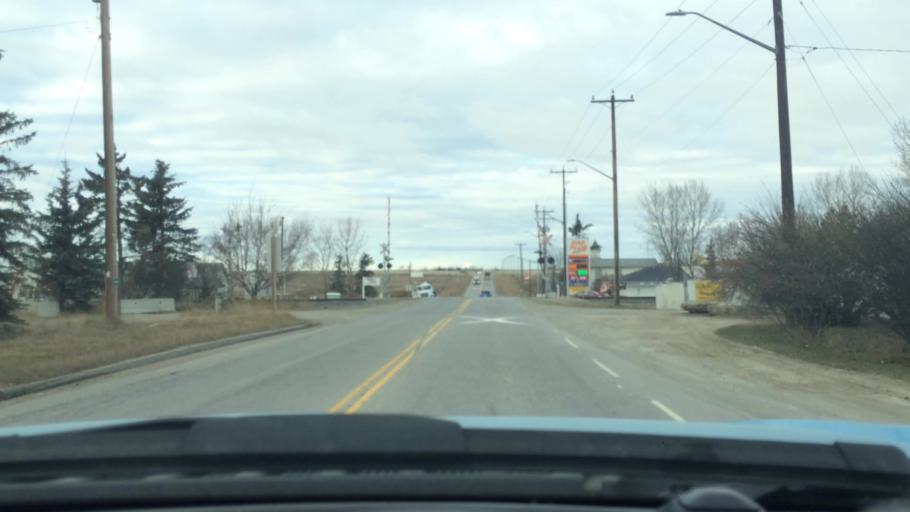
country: CA
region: Alberta
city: Airdrie
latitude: 51.2127
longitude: -114.0066
